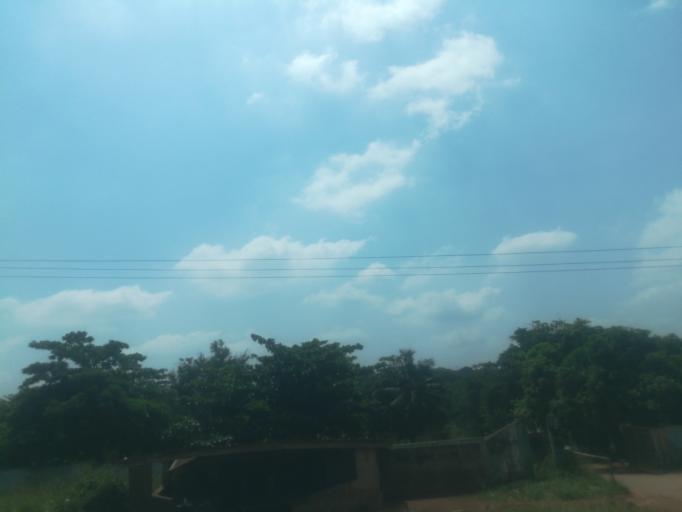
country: NG
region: Ogun
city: Abeokuta
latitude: 7.1406
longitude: 3.3979
